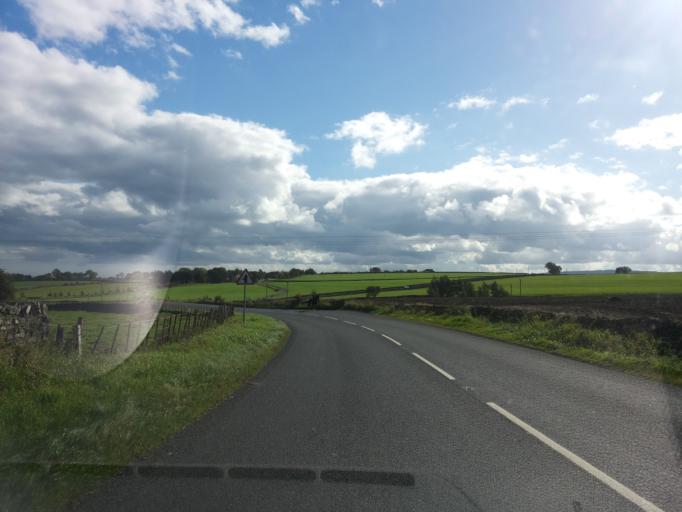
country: GB
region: England
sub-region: North Yorkshire
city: Leyburn
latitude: 54.3249
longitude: -1.8244
